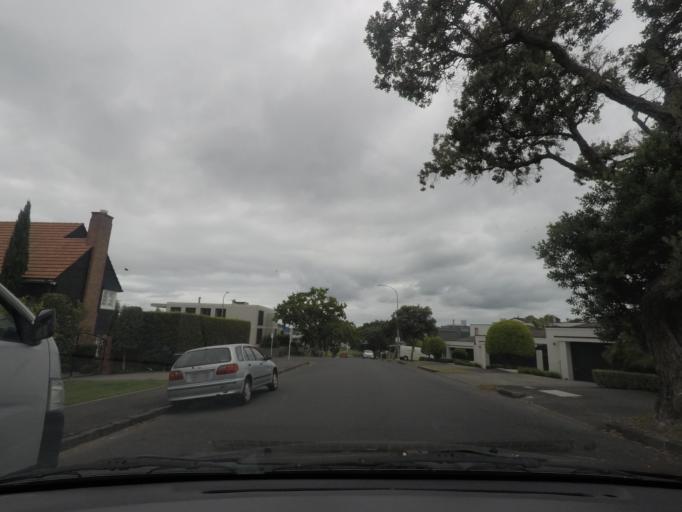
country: NZ
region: Auckland
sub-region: Auckland
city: Auckland
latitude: -36.8513
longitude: 174.7909
